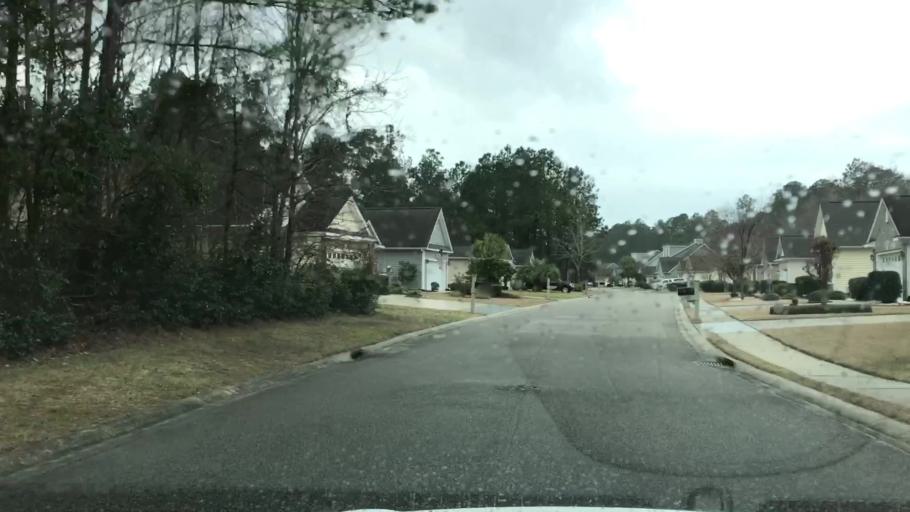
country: US
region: South Carolina
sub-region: Horry County
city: Red Hill
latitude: 33.7777
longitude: -79.0097
